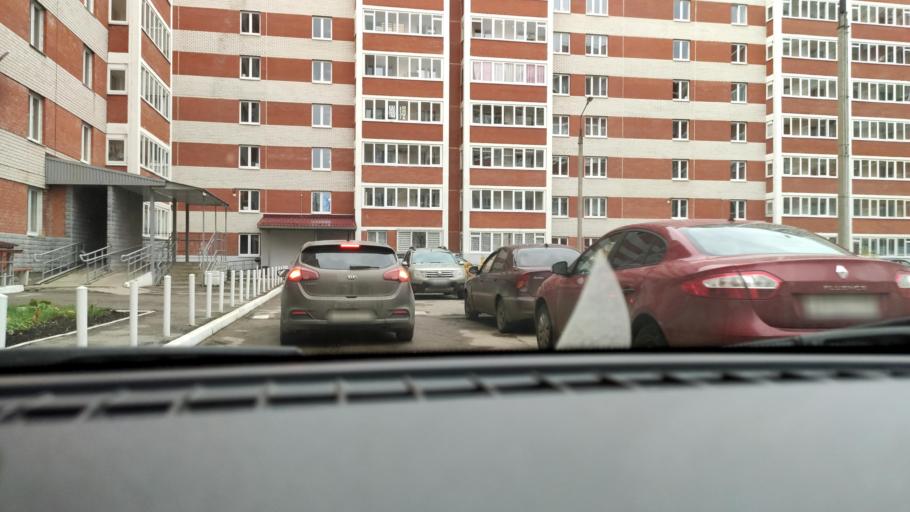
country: RU
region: Perm
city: Perm
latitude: 57.9955
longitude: 56.1807
